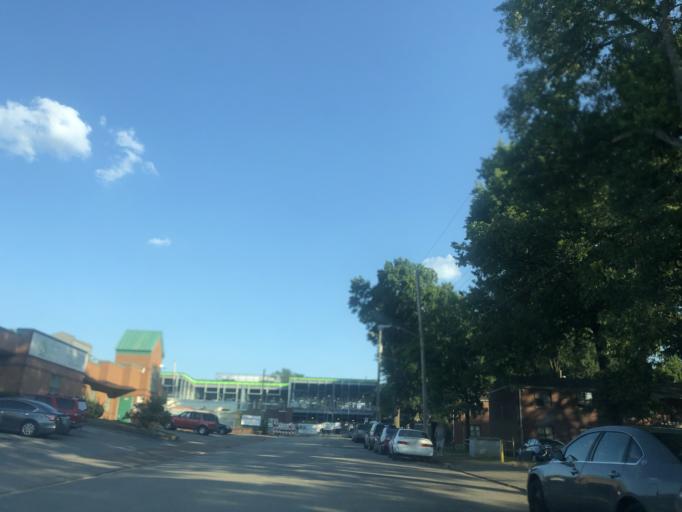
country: US
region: Tennessee
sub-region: Davidson County
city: Nashville
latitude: 36.1681
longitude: -86.7551
